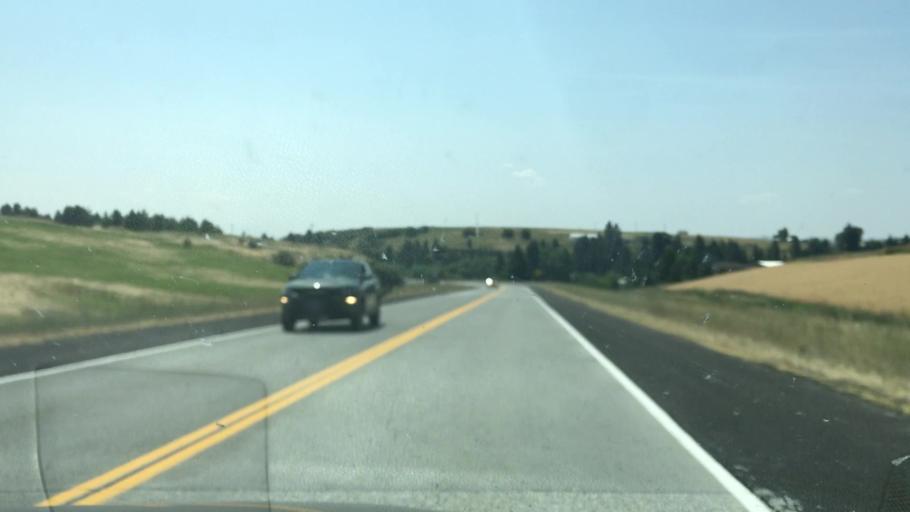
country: US
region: Idaho
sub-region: Lewis County
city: Nezperce
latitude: 46.0512
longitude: -116.3449
